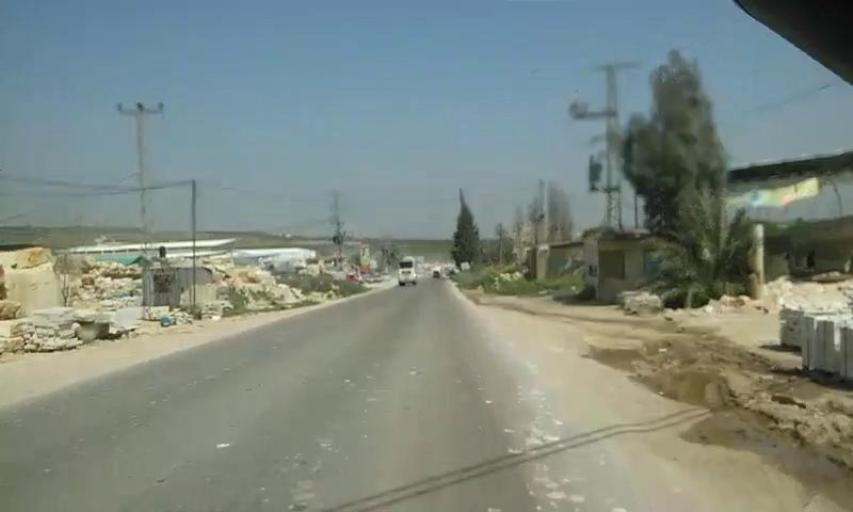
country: PS
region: West Bank
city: Ash Shuhada'
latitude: 32.4353
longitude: 35.2713
